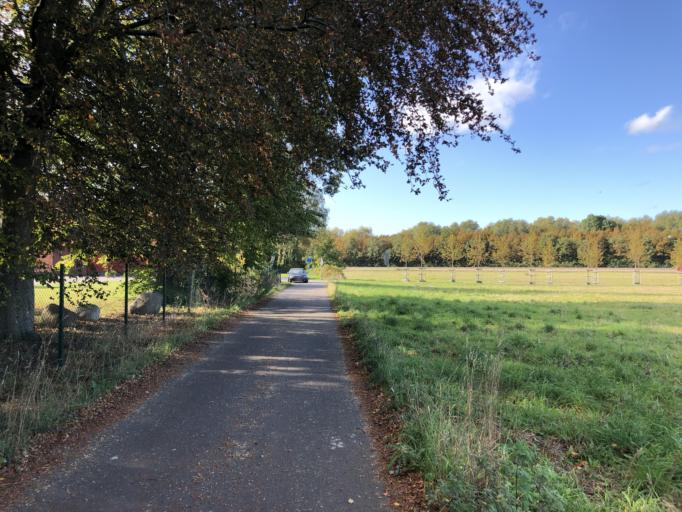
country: SE
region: Skane
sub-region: Lunds Kommun
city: Lund
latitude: 55.6887
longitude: 13.2071
